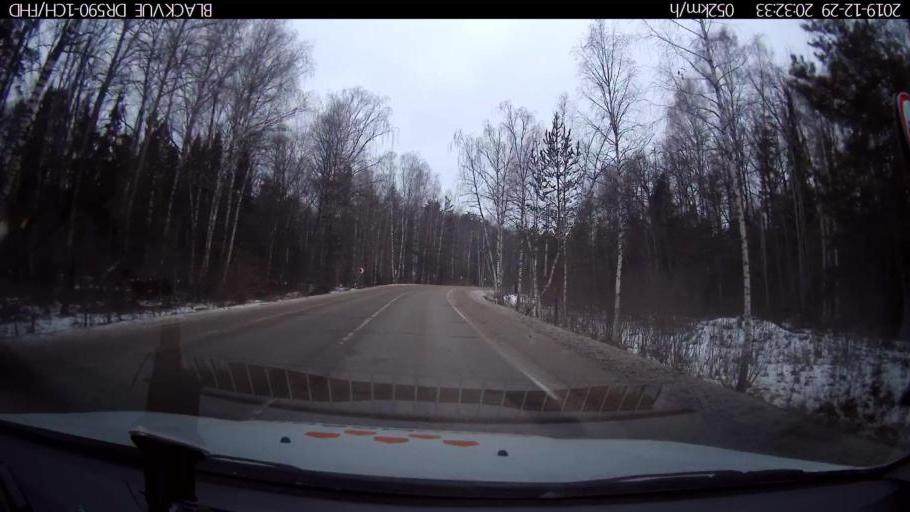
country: RU
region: Nizjnij Novgorod
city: Afonino
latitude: 56.1761
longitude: 44.0624
